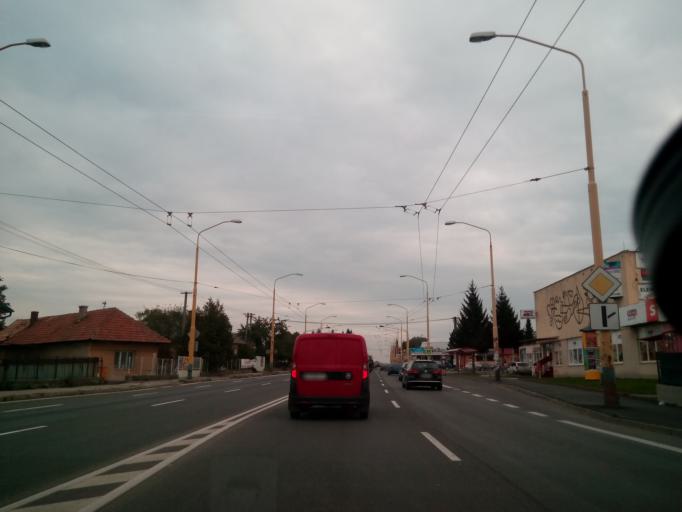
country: SK
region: Presovsky
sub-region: Okres Presov
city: Presov
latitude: 49.0228
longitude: 21.2802
